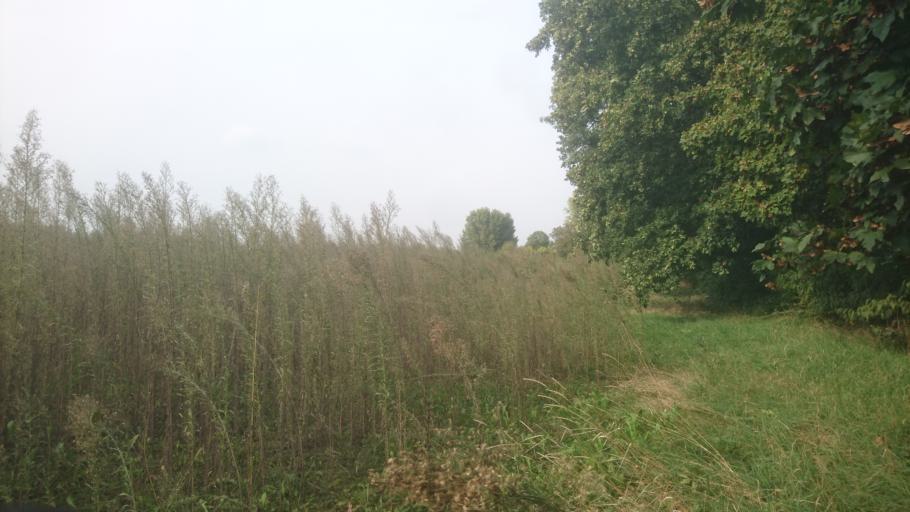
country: IT
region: Veneto
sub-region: Provincia di Vicenza
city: Montegalda
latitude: 45.4620
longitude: 11.6671
